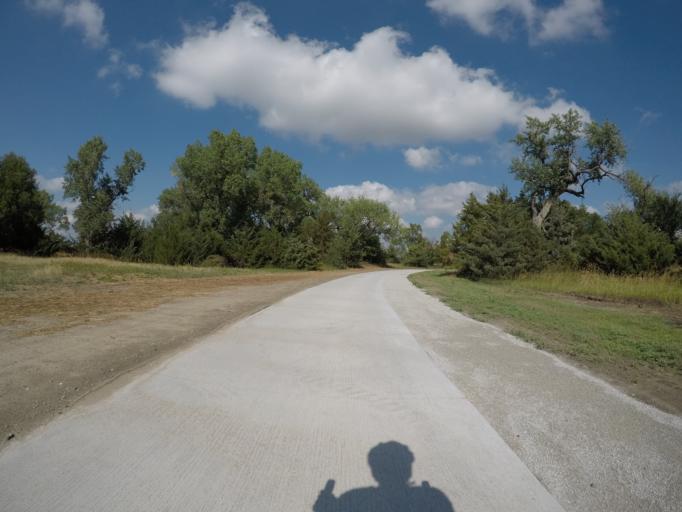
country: US
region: Nebraska
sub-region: Buffalo County
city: Kearney
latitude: 40.6735
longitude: -99.0211
